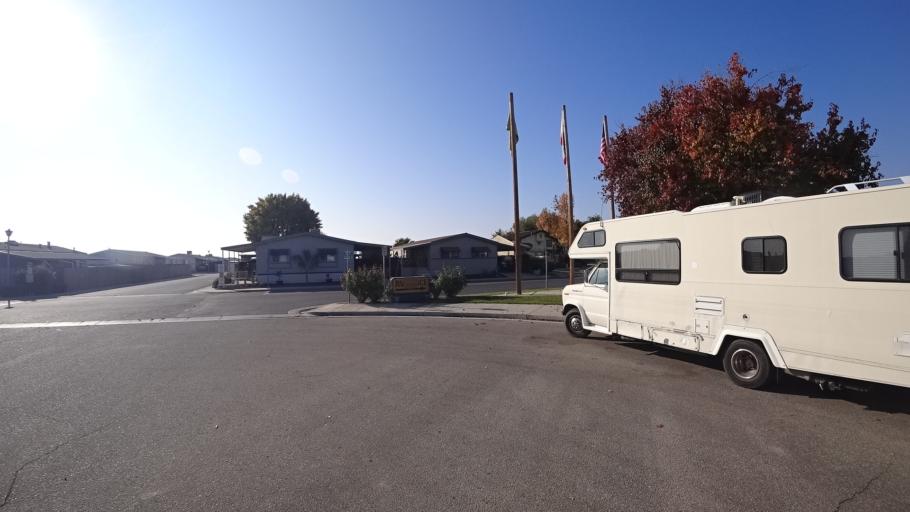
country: US
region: California
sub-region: Kern County
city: Greenfield
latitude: 35.2653
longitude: -119.0193
